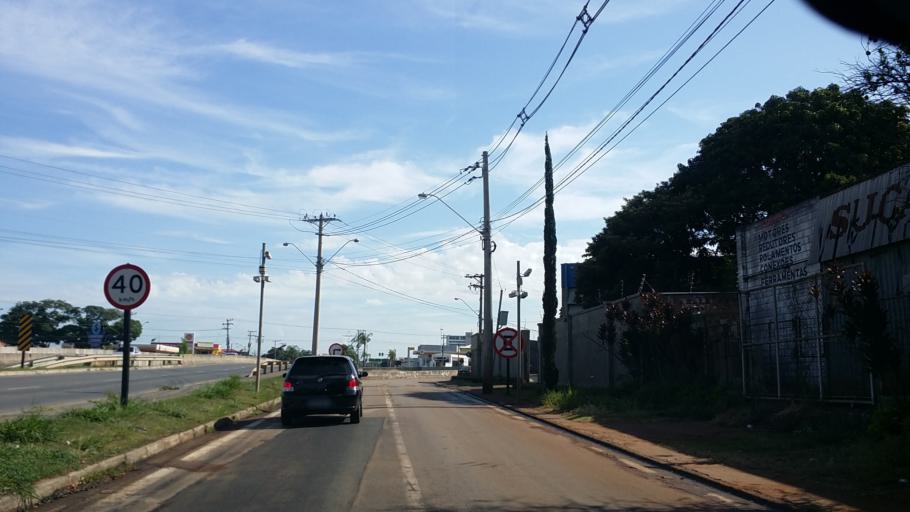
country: BR
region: Sao Paulo
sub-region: Indaiatuba
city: Indaiatuba
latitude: -23.1249
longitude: -47.2256
